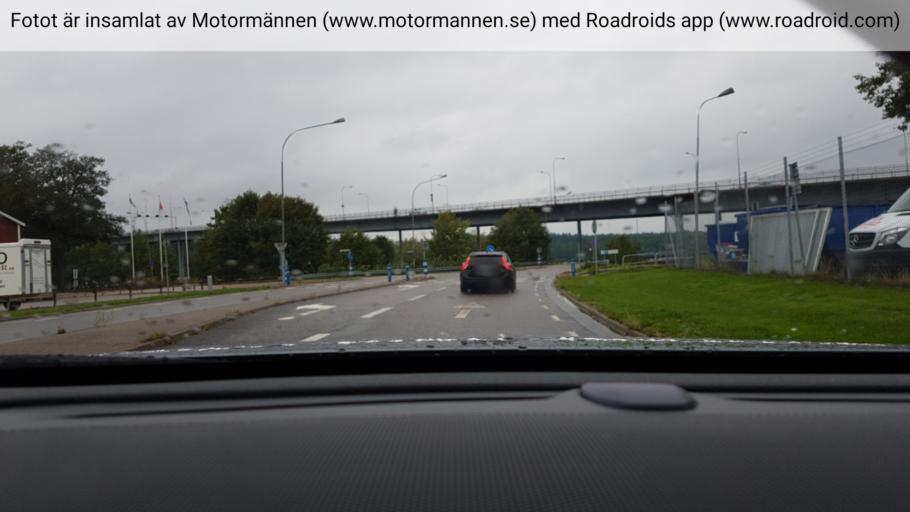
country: SE
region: Vaestra Goetaland
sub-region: Vanersborgs Kommun
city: Vanersborg
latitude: 58.3809
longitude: 12.3156
